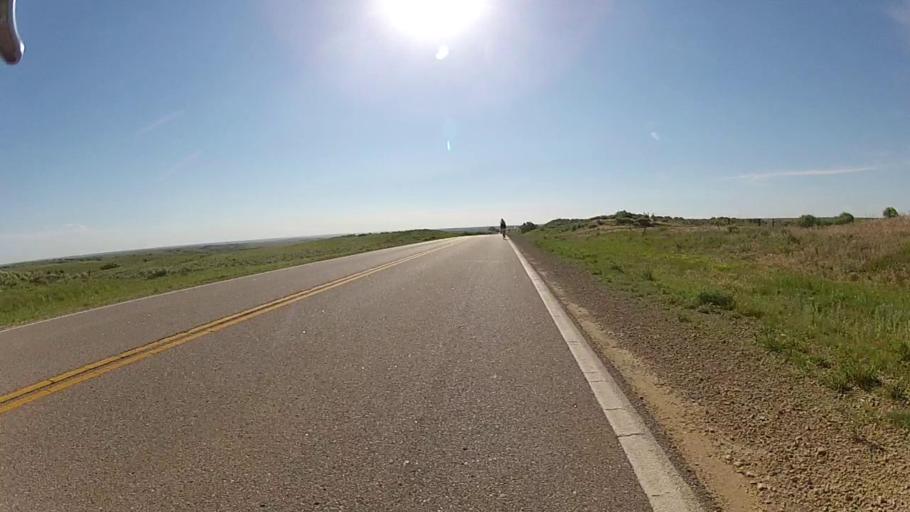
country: US
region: Kansas
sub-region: Barber County
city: Medicine Lodge
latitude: 37.2816
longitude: -98.8983
